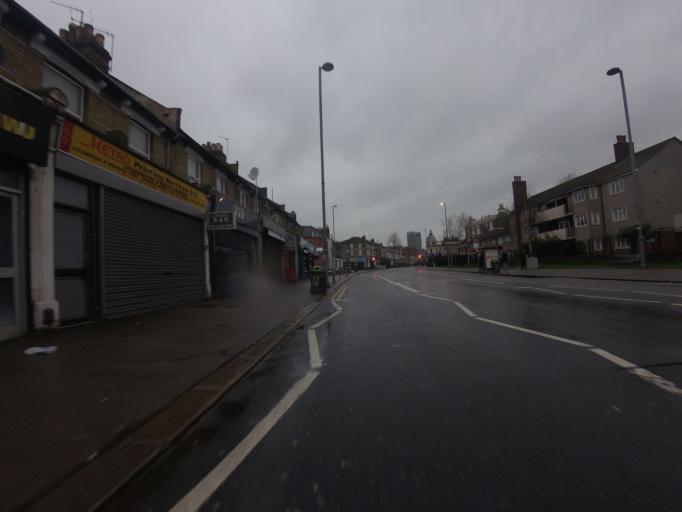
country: GB
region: England
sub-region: Greater London
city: Walthamstow
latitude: 51.5793
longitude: -0.0180
